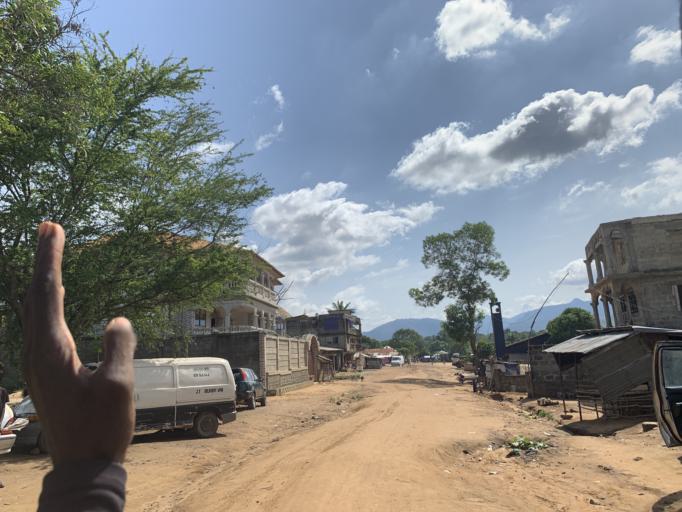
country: SL
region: Western Area
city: Waterloo
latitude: 8.3313
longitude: -13.0509
